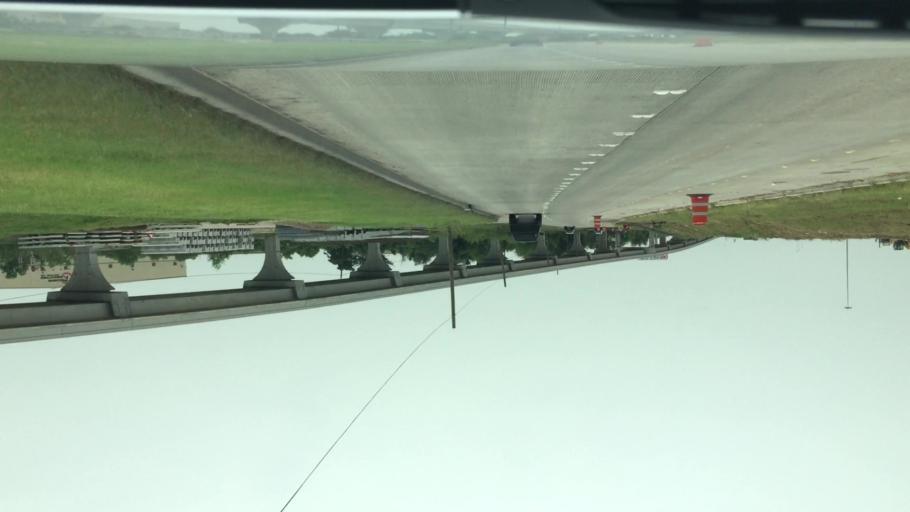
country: US
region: Texas
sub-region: Harris County
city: Oak Cliff Place
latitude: 29.9105
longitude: -95.6126
